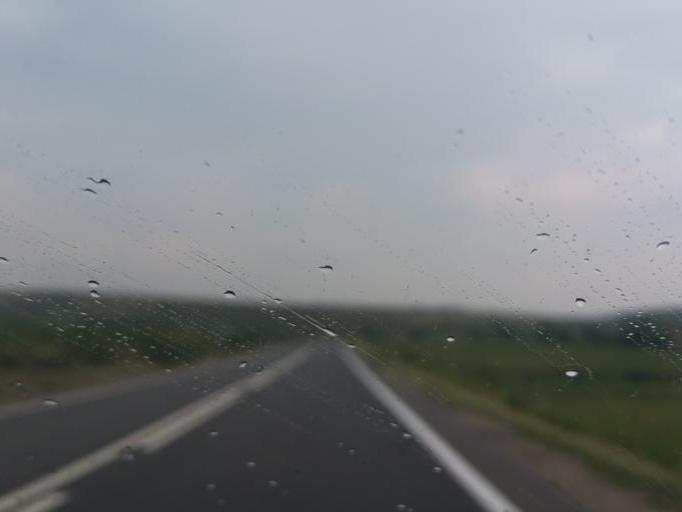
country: RO
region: Cluj
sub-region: Comuna Sanpaul
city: Sanpaul
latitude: 46.9210
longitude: 23.4148
